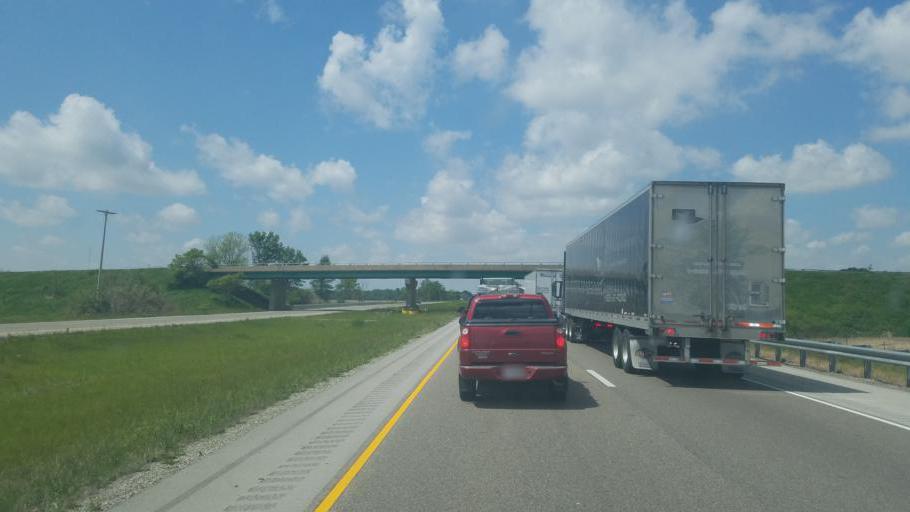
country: US
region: Illinois
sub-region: Cumberland County
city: Toledo
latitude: 39.2293
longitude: -88.2191
